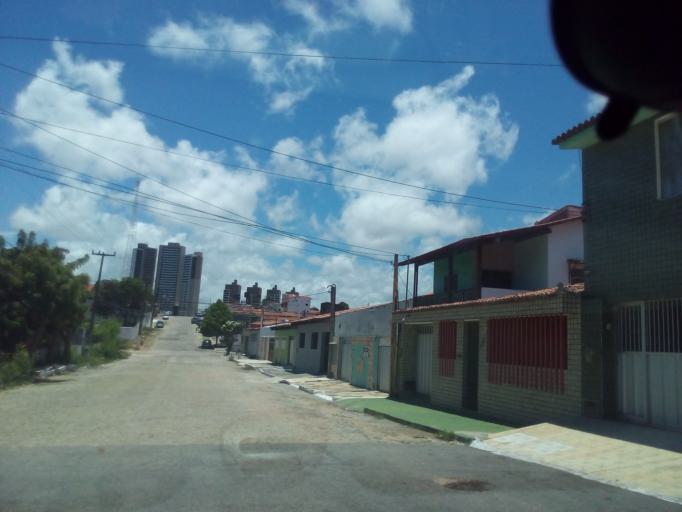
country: BR
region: Rio Grande do Norte
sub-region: Natal
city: Natal
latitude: -5.8442
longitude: -35.2045
